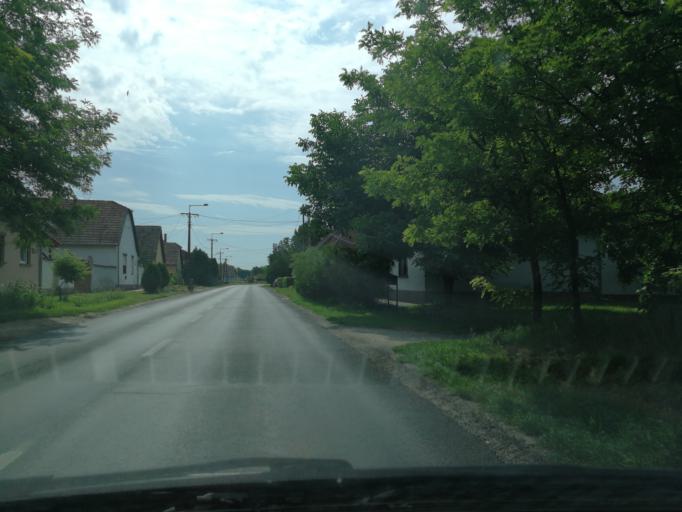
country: HU
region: Bacs-Kiskun
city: Nagybaracska
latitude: 46.0364
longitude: 18.9315
